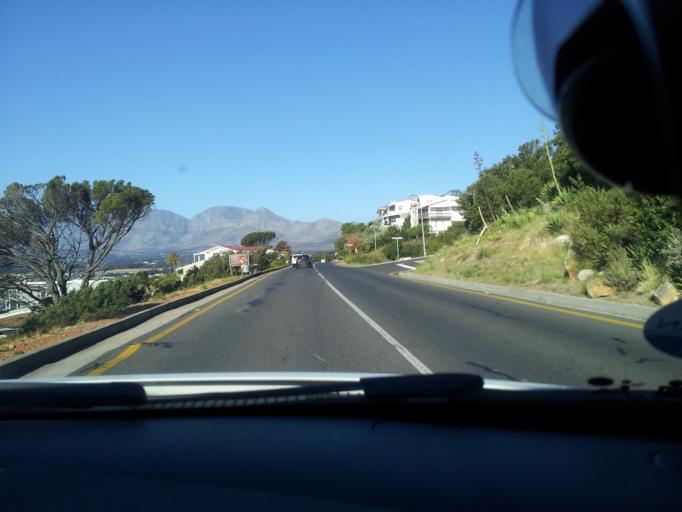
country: ZA
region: Western Cape
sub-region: Overberg District Municipality
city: Grabouw
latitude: -34.1659
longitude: 18.8609
